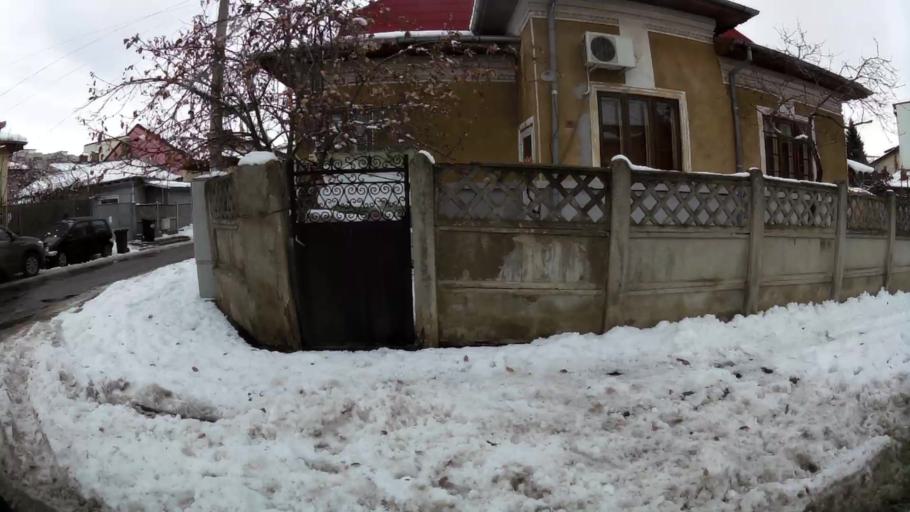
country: RO
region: Bucuresti
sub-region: Municipiul Bucuresti
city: Bucuresti
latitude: 44.3980
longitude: 26.1000
